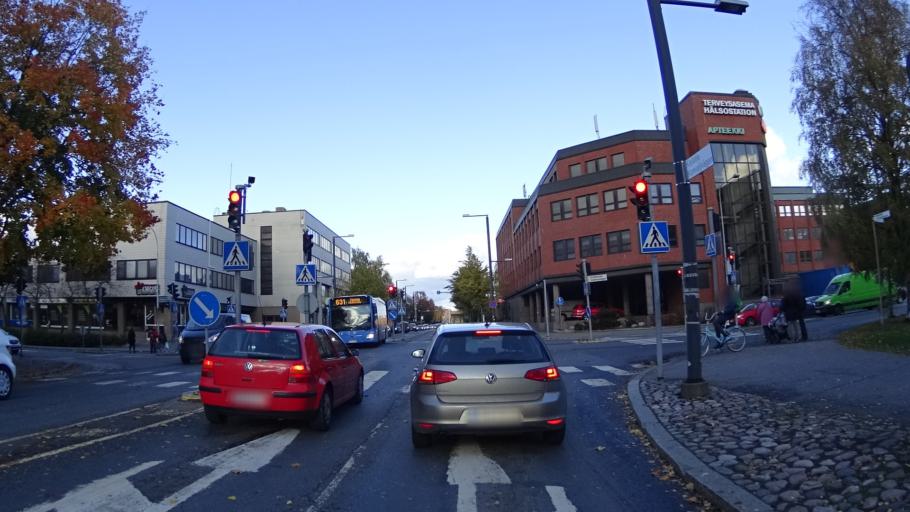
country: FI
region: Uusimaa
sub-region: Helsinki
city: Vantaa
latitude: 60.2921
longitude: 25.0371
